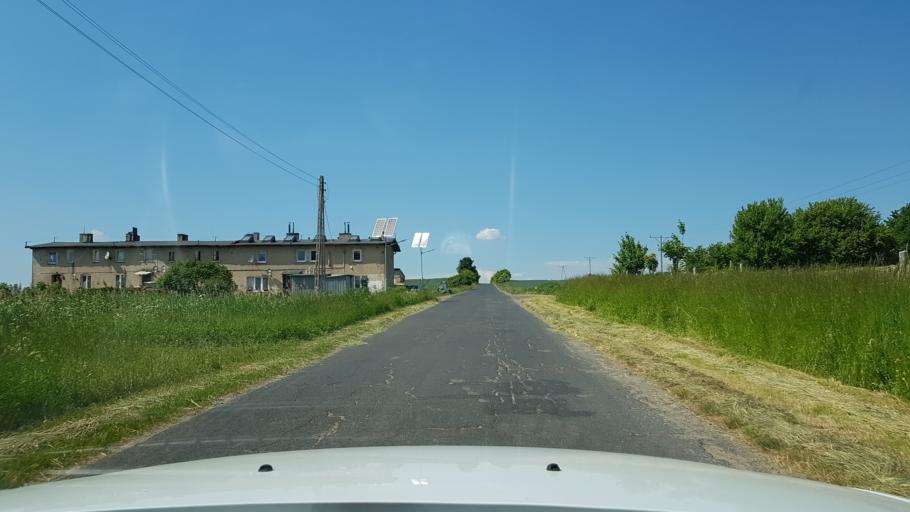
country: PL
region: West Pomeranian Voivodeship
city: Trzcinsko Zdroj
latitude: 53.0007
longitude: 14.5698
